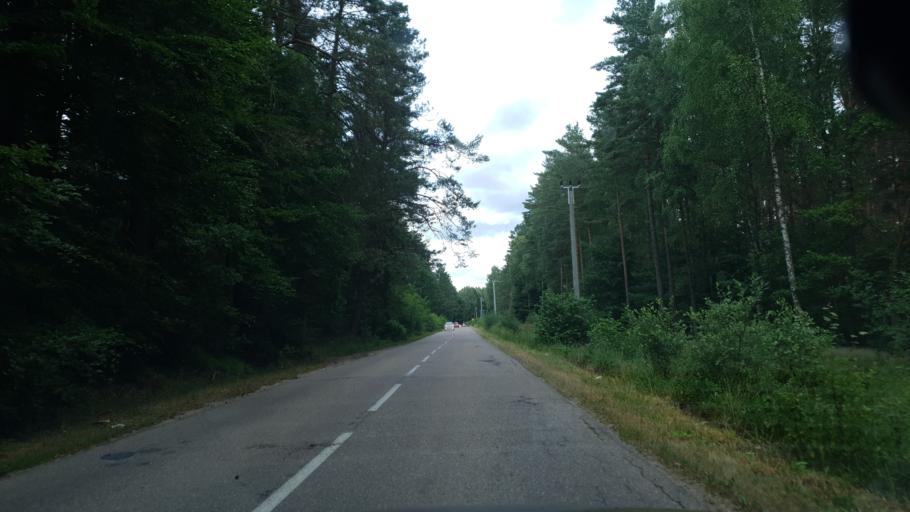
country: PL
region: Pomeranian Voivodeship
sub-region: Powiat kartuski
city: Stezyca
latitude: 54.2537
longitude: 18.0144
